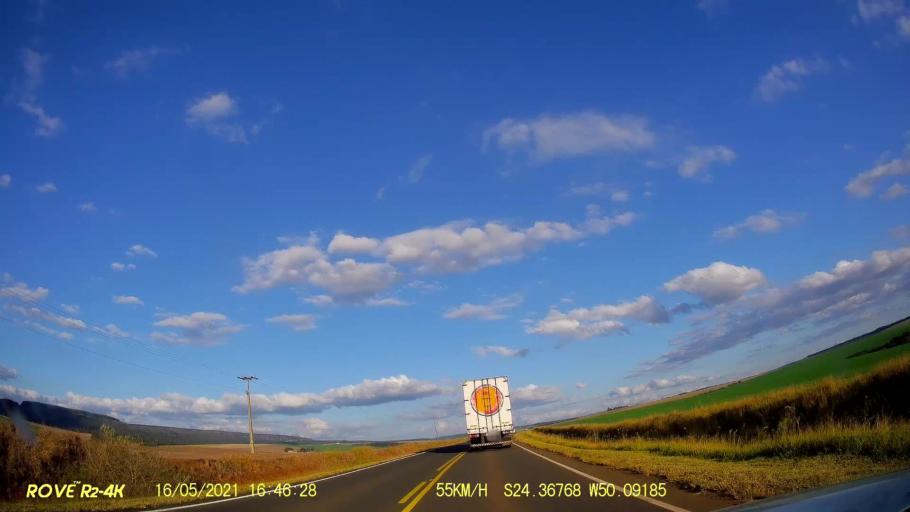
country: BR
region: Parana
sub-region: Pirai Do Sul
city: Pirai do Sul
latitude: -24.3678
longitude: -50.0915
